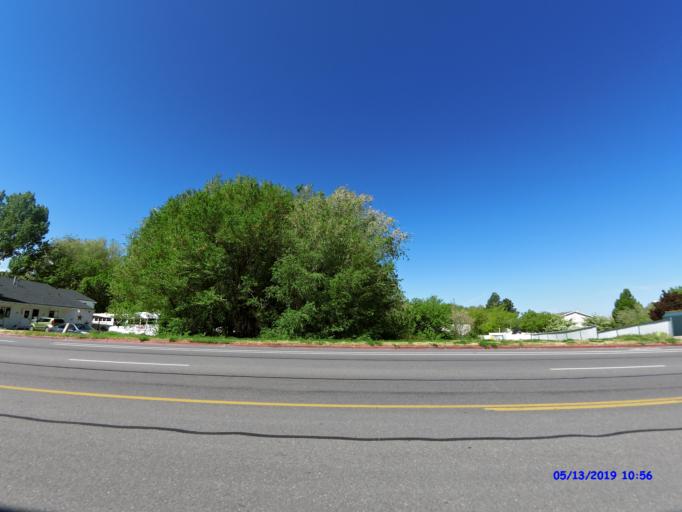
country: US
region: Utah
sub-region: Weber County
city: Ogden
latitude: 41.2431
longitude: -111.9534
